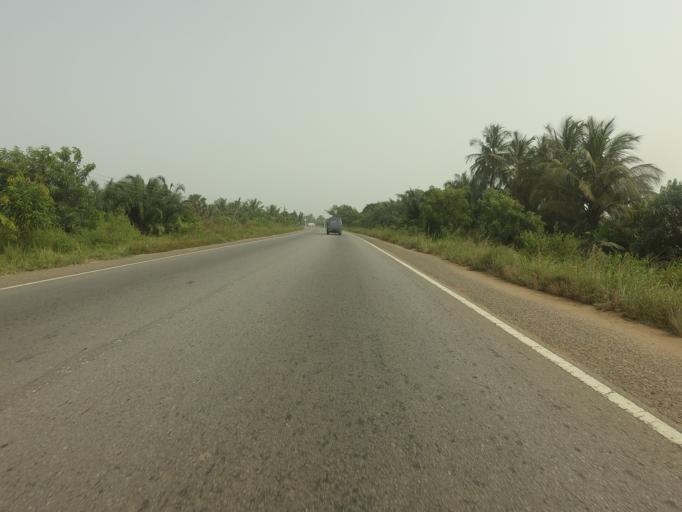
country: GH
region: Volta
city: Anloga
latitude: 5.9923
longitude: 0.5691
